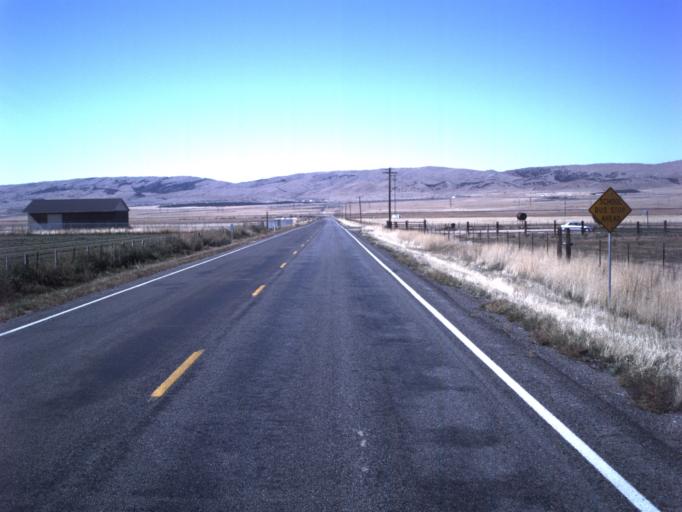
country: US
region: Utah
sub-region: Juab County
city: Nephi
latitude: 39.5581
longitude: -111.8895
